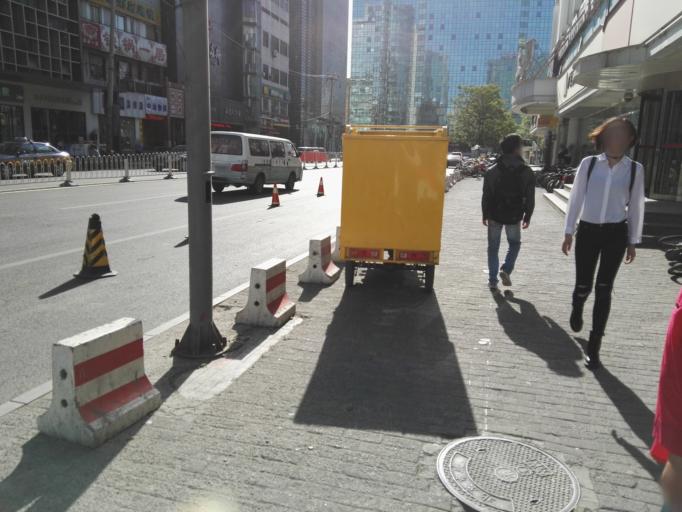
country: CN
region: Beijing
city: Haidian
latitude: 39.9814
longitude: 116.3021
